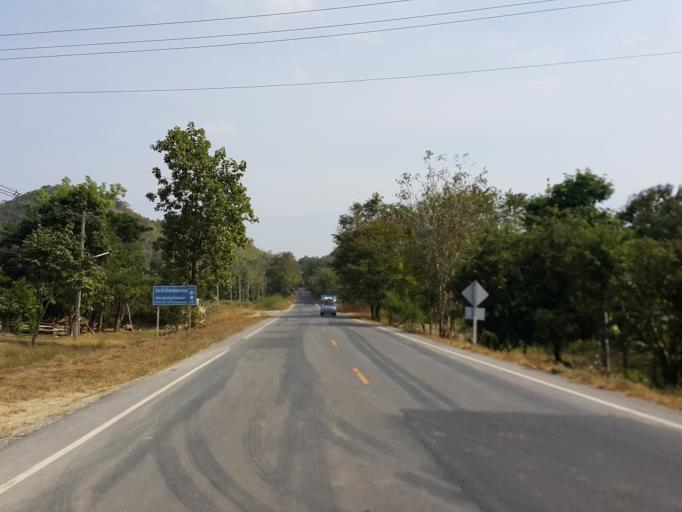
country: TH
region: Sukhothai
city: Thung Saliam
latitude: 17.3449
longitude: 99.4461
